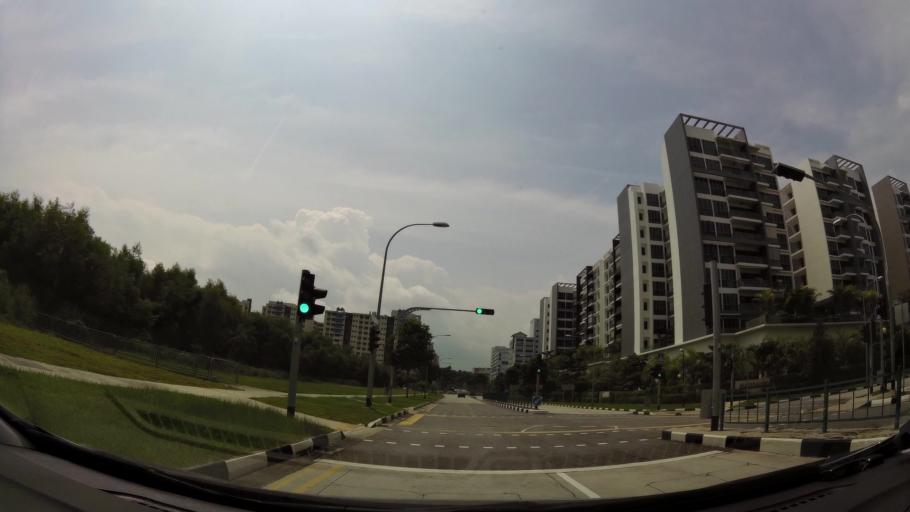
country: MY
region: Johor
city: Kampung Pasir Gudang Baru
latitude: 1.3769
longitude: 103.9618
